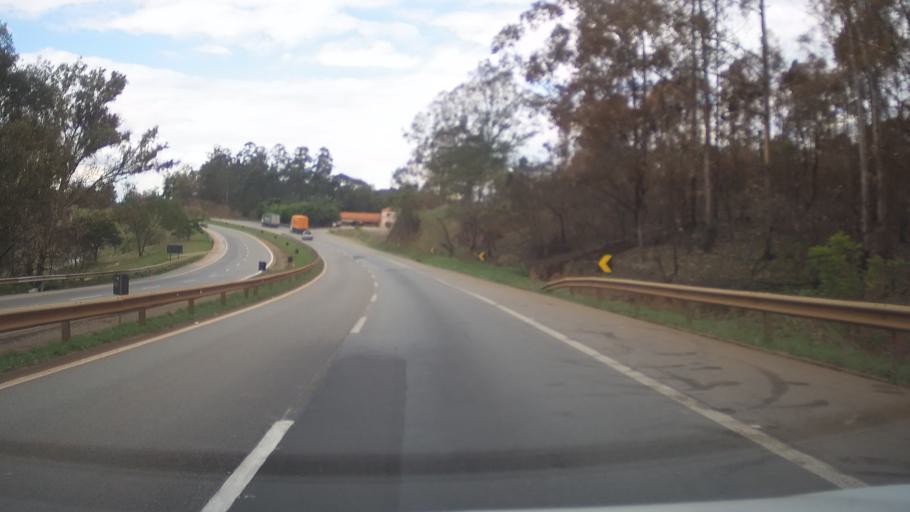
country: BR
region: Minas Gerais
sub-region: Itauna
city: Itauna
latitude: -20.2961
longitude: -44.4382
